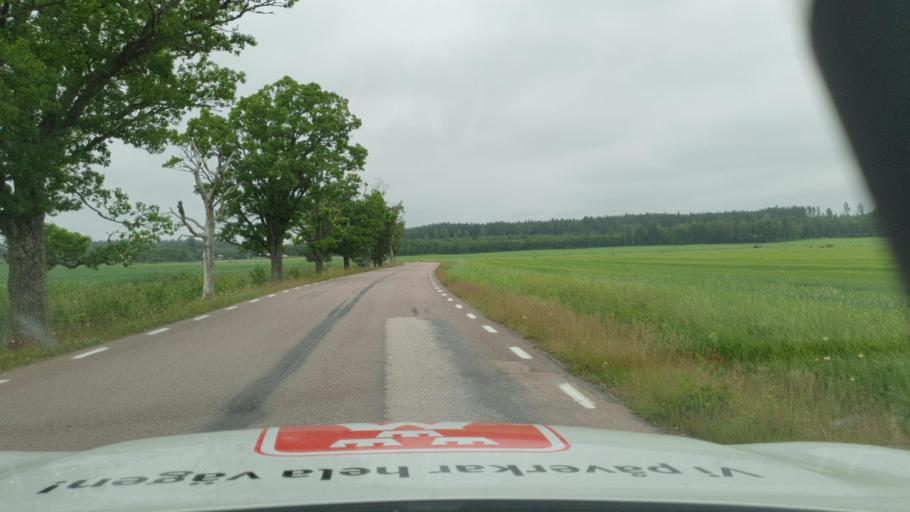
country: SE
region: Vaermland
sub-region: Karlstads Kommun
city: Skattkarr
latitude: 59.4109
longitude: 13.8730
